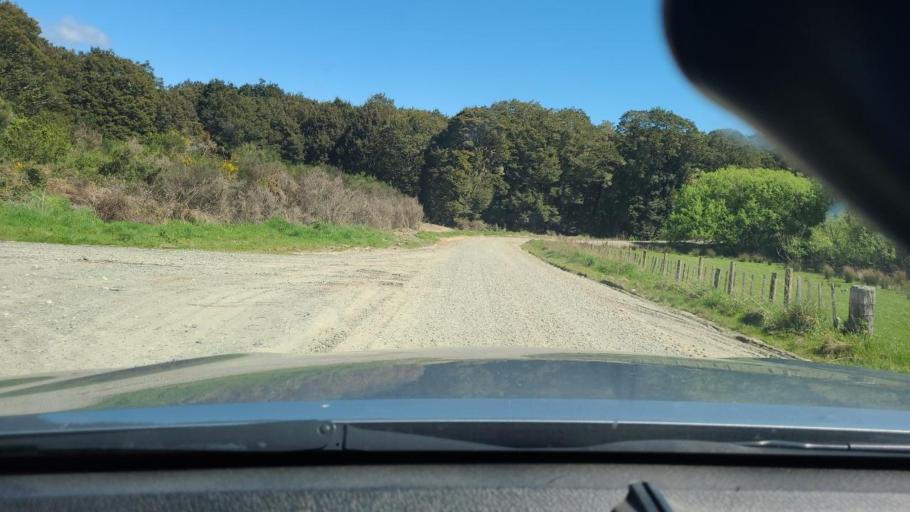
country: NZ
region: Southland
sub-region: Southland District
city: Riverton
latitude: -46.1002
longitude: 167.6027
